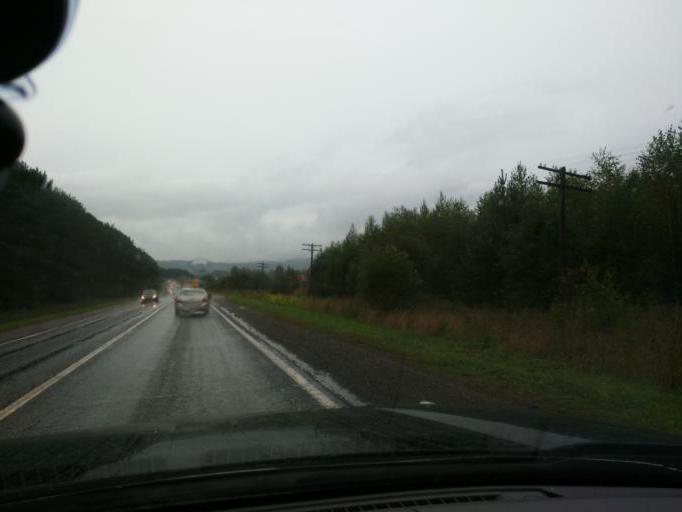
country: RU
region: Perm
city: Yugo-Kamskiy
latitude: 57.6789
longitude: 55.5766
